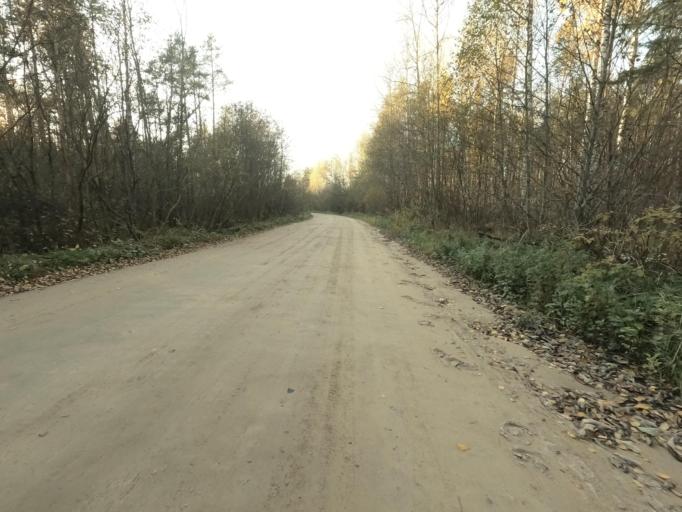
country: RU
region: Leningrad
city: Kirovsk
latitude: 59.8792
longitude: 31.0332
